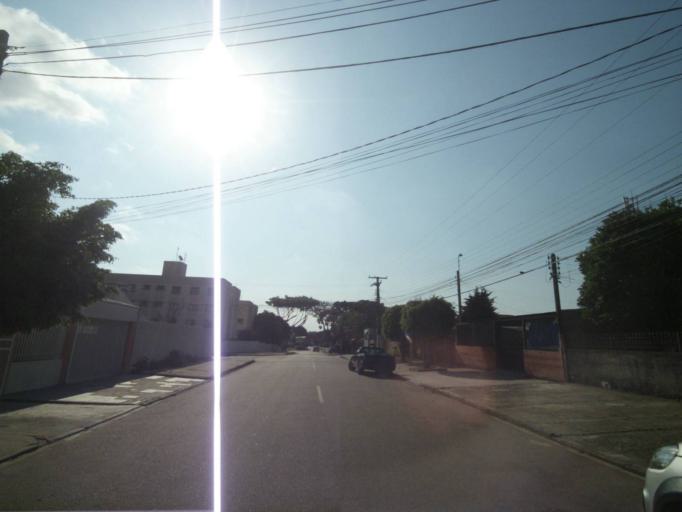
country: BR
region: Parana
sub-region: Curitiba
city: Curitiba
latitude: -25.4882
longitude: -49.3245
